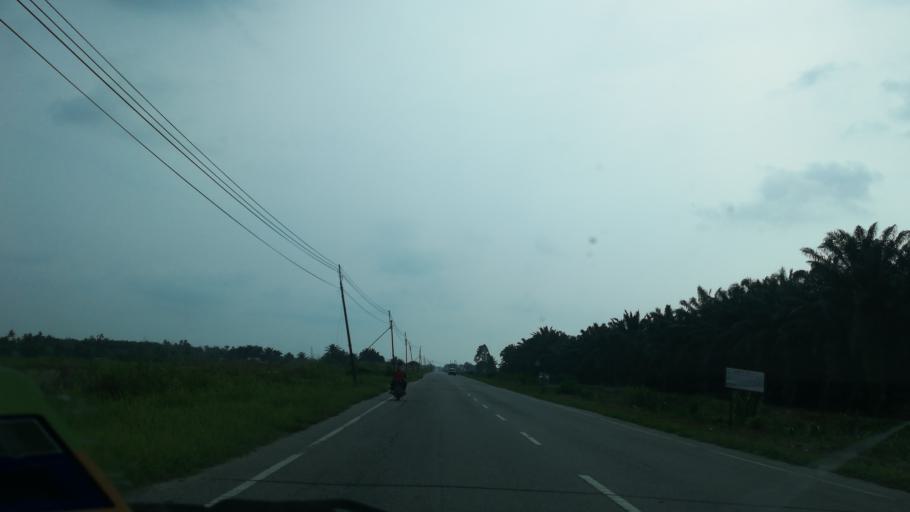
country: MY
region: Perak
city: Teluk Intan
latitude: 4.1093
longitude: 101.0634
